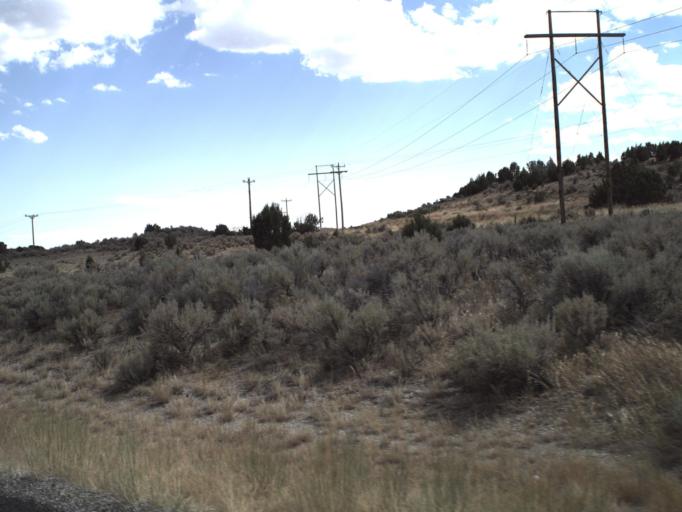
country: US
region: Idaho
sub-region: Minidoka County
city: Rupert
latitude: 41.9769
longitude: -113.1614
